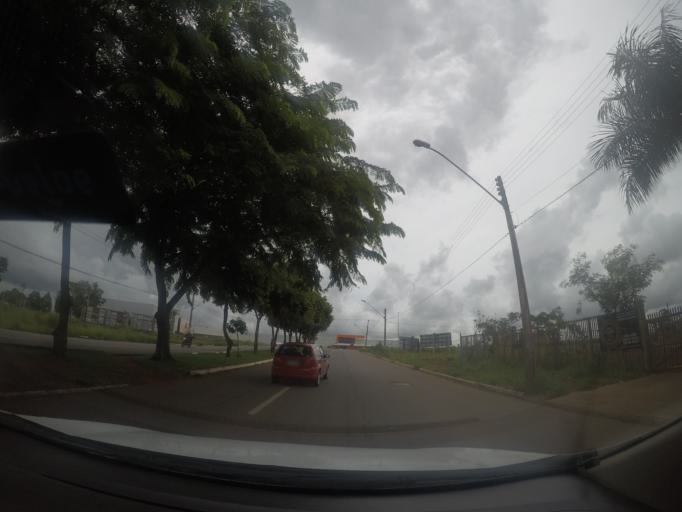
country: BR
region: Goias
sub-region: Trindade
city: Trindade
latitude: -16.6568
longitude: -49.3849
